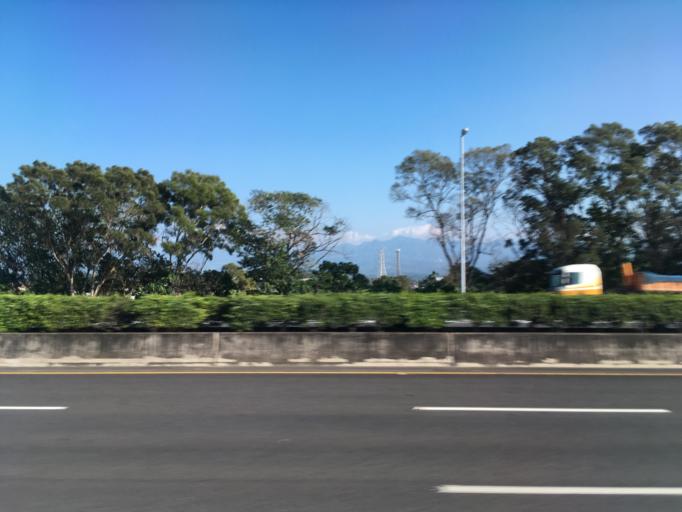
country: TW
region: Taiwan
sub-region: Chiayi
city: Jiayi Shi
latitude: 23.4465
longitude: 120.4827
